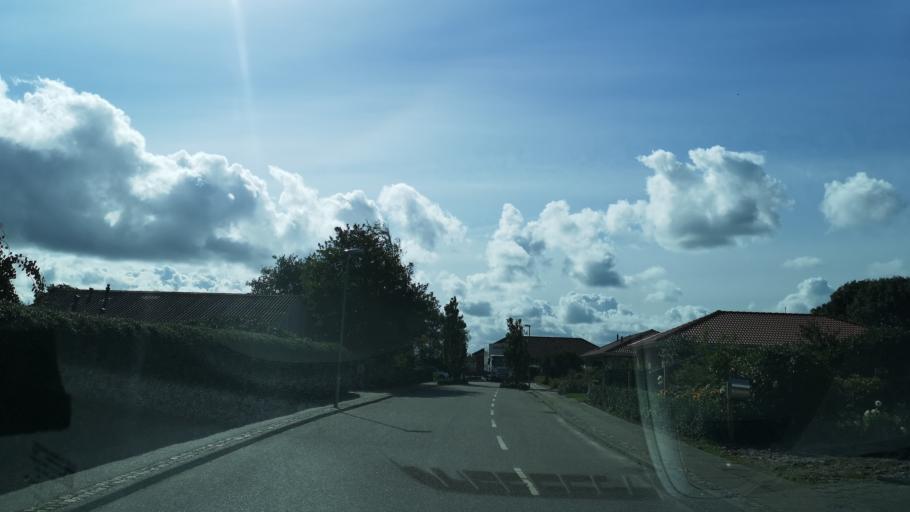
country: DK
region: Central Jutland
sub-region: Ringkobing-Skjern Kommune
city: Skjern
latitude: 55.9837
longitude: 8.5442
